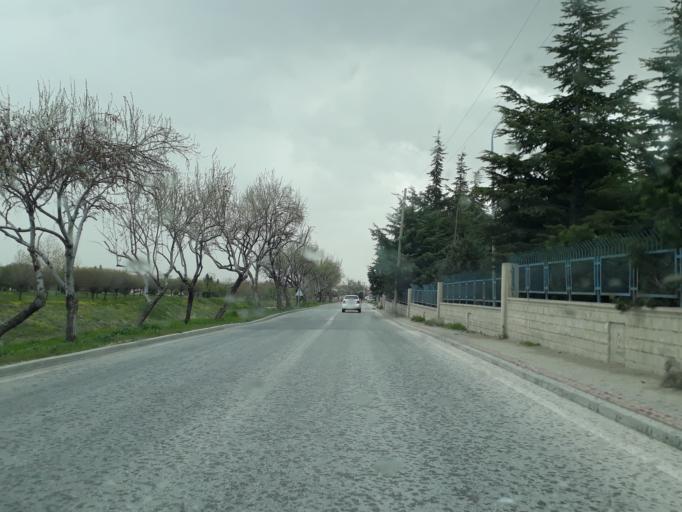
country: TR
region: Konya
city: Selcuklu
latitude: 37.9183
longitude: 32.4727
